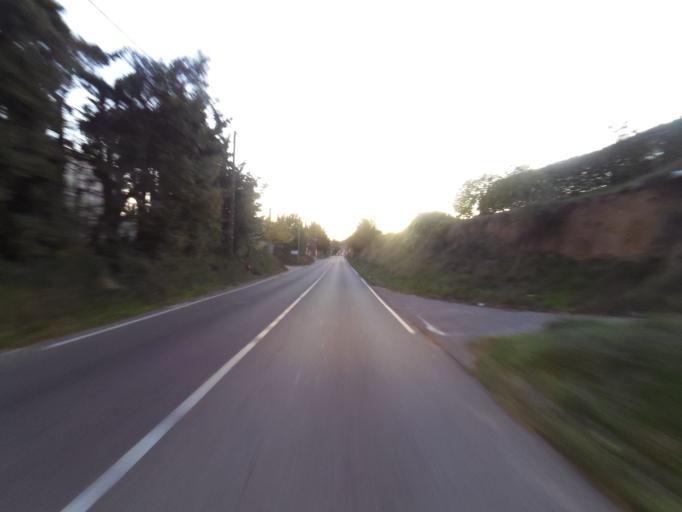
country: FR
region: Provence-Alpes-Cote d'Azur
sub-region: Departement du Vaucluse
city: Carpentras
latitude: 44.0656
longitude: 5.0655
